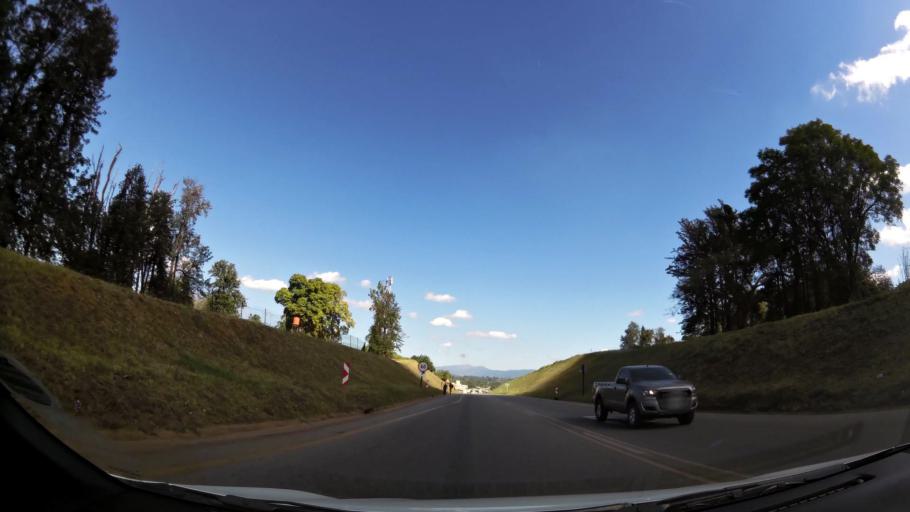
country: ZA
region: Limpopo
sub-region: Mopani District Municipality
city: Tzaneen
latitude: -23.8148
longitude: 30.1728
